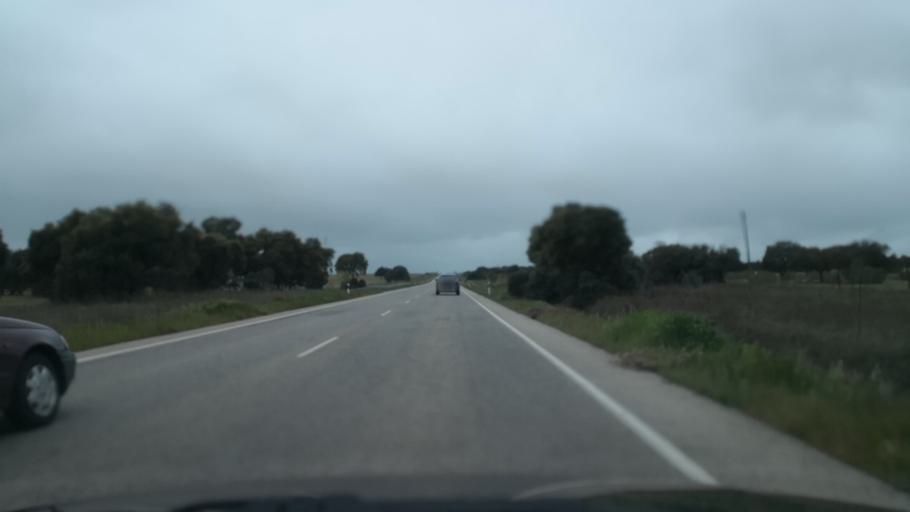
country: ES
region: Extremadura
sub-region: Provincia de Caceres
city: Malpartida de Caceres
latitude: 39.3688
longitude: -6.4573
